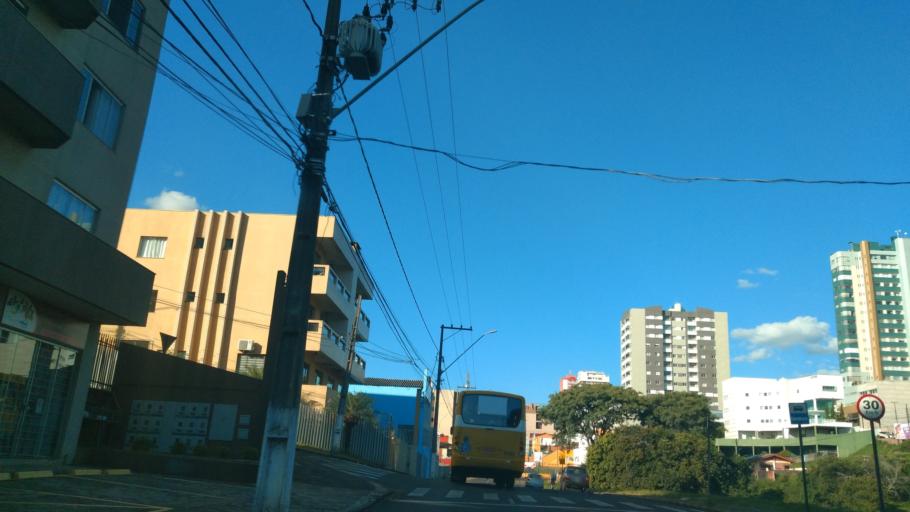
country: BR
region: Parana
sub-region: Guarapuava
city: Guarapuava
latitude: -25.3974
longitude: -51.4720
